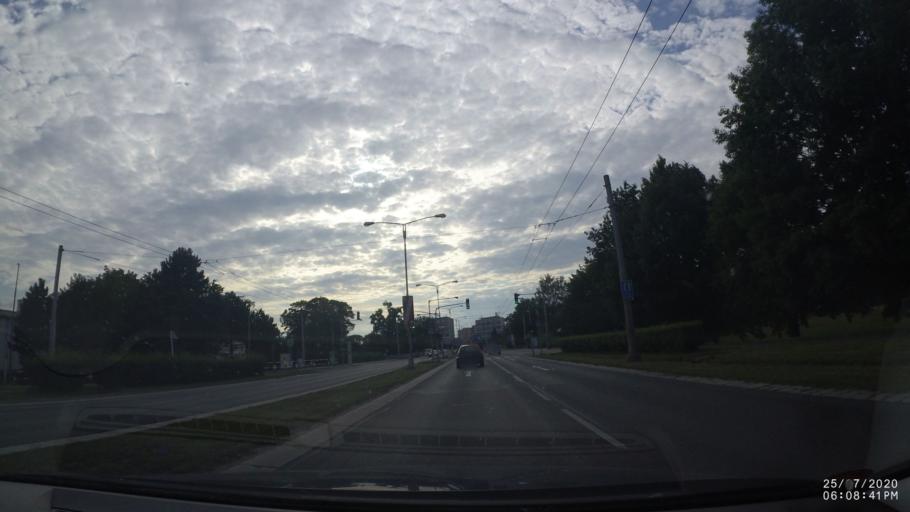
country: CZ
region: Kralovehradecky
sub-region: Okres Hradec Kralove
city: Hradec Kralove
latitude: 50.2020
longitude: 15.8269
